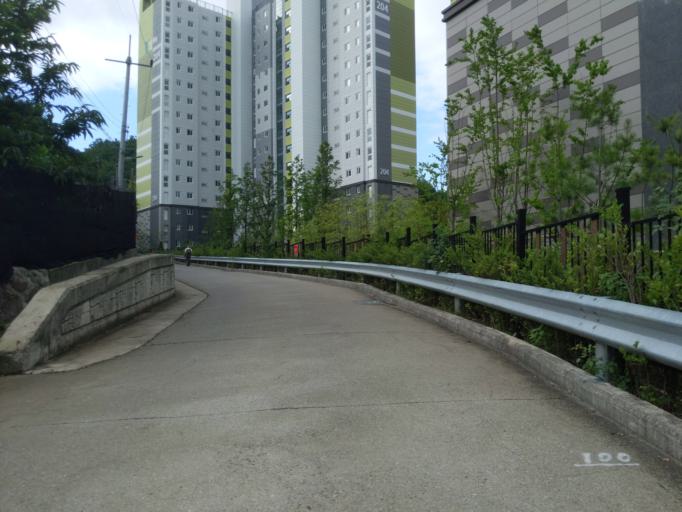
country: KR
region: Daegu
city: Hwawon
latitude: 35.7990
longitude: 128.5324
